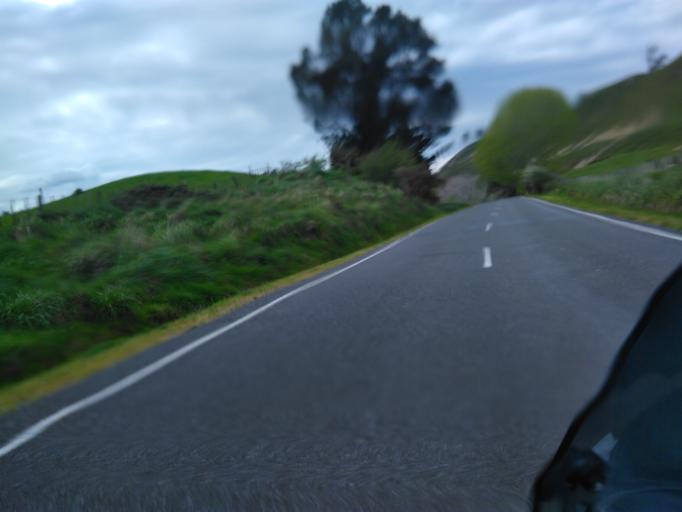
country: NZ
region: Hawke's Bay
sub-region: Wairoa District
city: Wairoa
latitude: -38.9234
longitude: 177.4294
